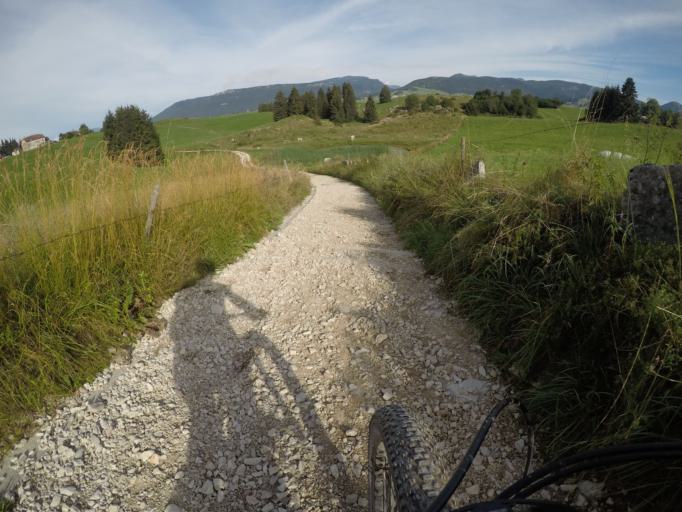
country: IT
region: Veneto
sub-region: Provincia di Vicenza
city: Asiago
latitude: 45.8561
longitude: 11.5104
